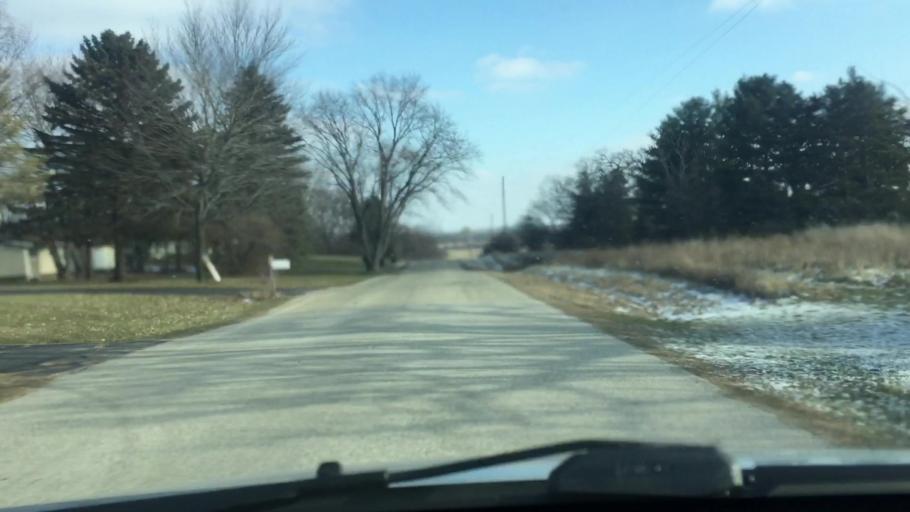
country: US
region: Wisconsin
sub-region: Jefferson County
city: Palmyra
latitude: 42.9008
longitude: -88.5521
